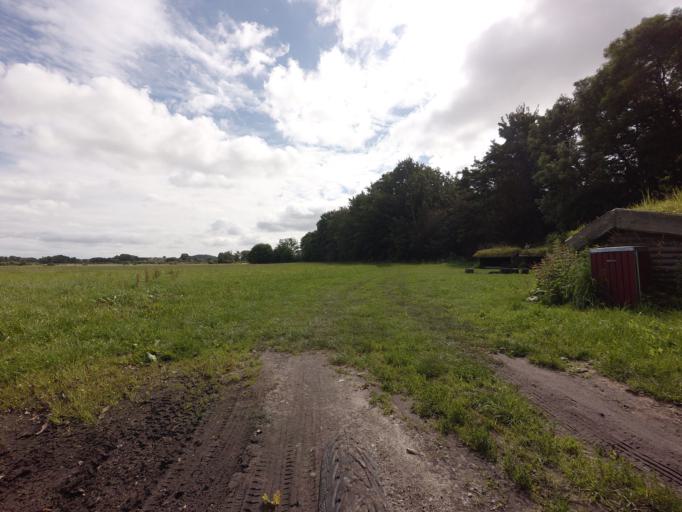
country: DK
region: Central Jutland
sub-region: Norddjurs Kommune
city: Allingabro
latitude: 56.4434
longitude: 10.3466
